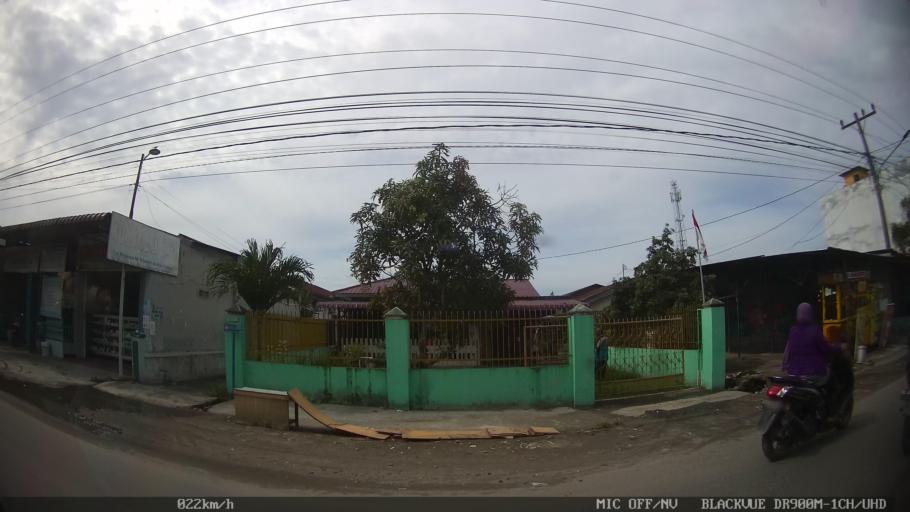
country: ID
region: North Sumatra
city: Medan
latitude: 3.6207
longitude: 98.7276
